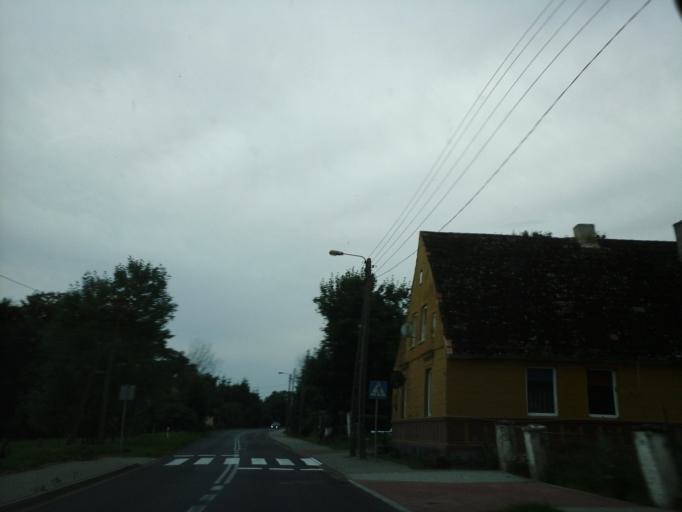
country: PL
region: West Pomeranian Voivodeship
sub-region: Powiat goleniowski
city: Nowogard
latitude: 53.5944
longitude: 15.1513
